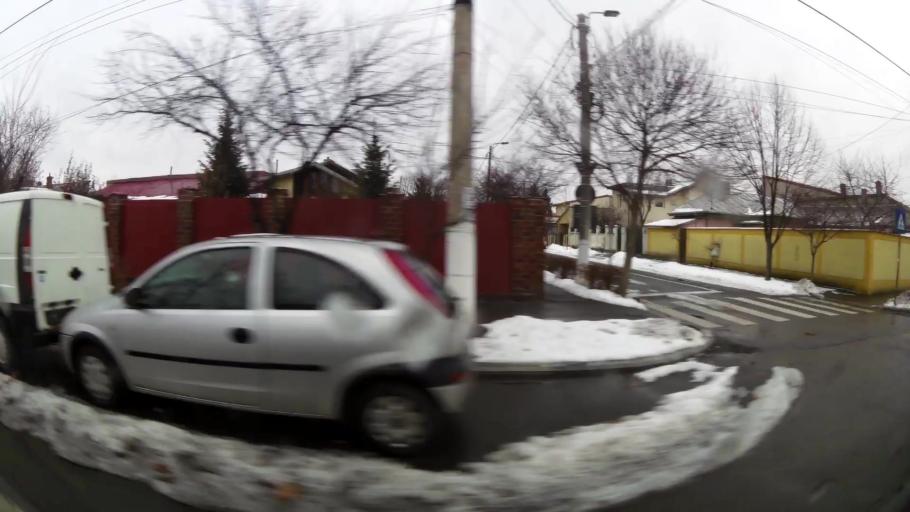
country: RO
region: Ilfov
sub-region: Comuna Chiajna
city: Rosu
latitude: 44.4907
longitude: 26.0208
